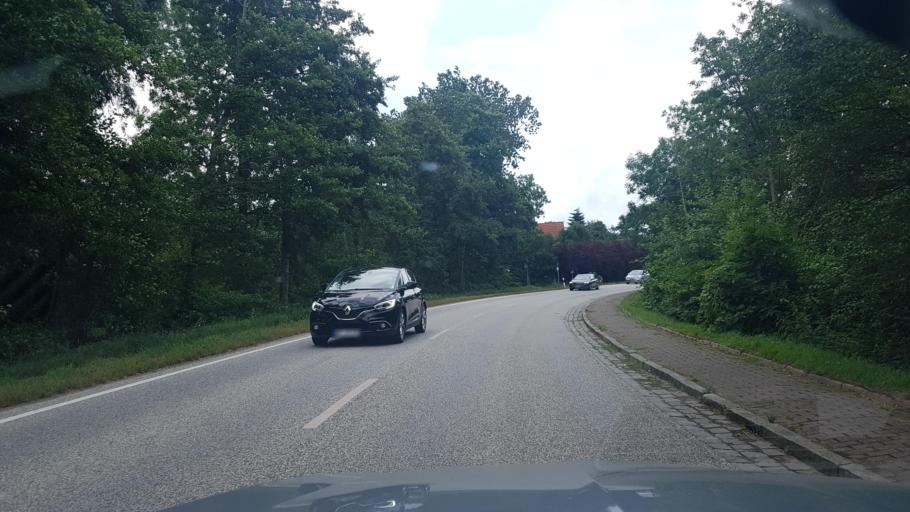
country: DE
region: Schleswig-Holstein
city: Tating
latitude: 54.3266
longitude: 8.7120
